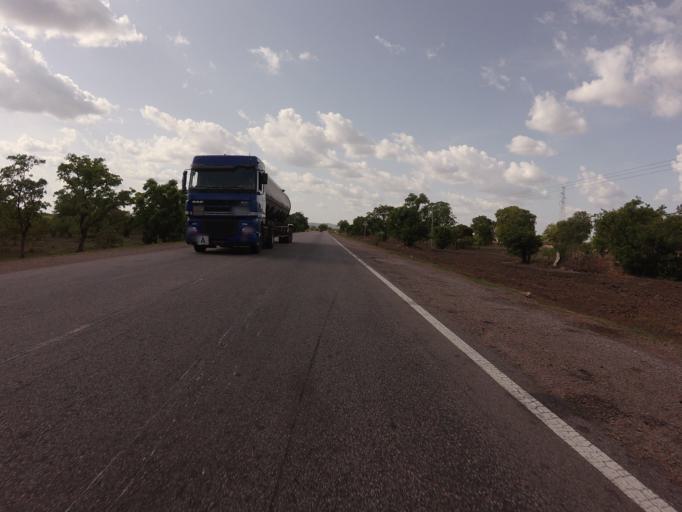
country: GH
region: Upper East
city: Bolgatanga
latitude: 10.5772
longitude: -0.8324
